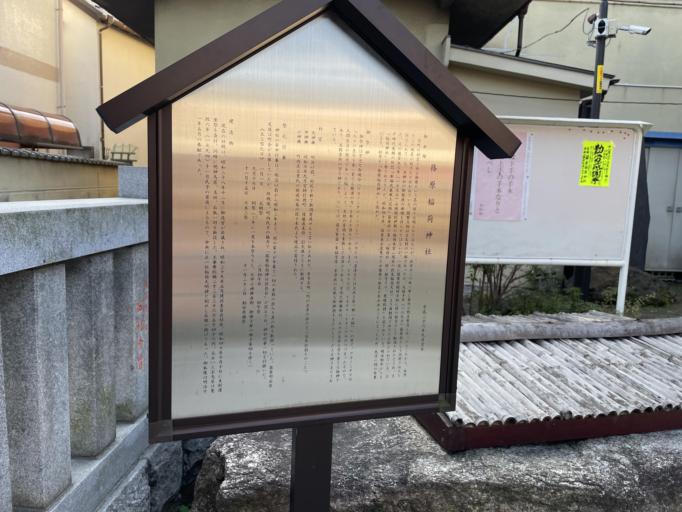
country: JP
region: Chiba
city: Matsudo
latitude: 35.7401
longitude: 139.8337
